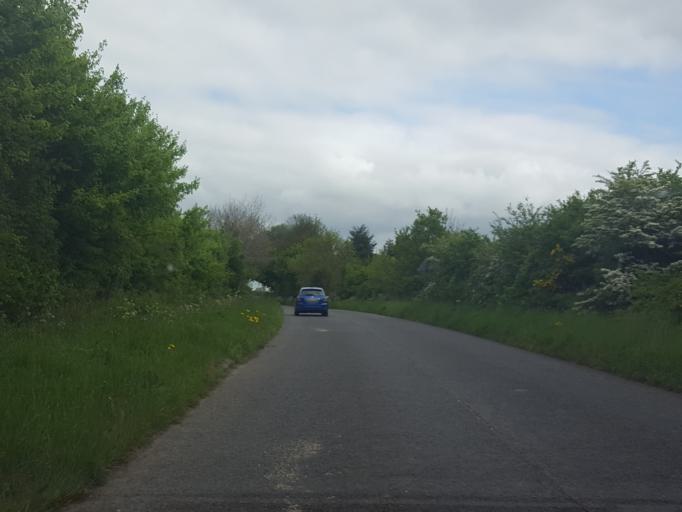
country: GB
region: England
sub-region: Essex
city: Little Clacton
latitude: 51.8402
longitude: 1.1231
